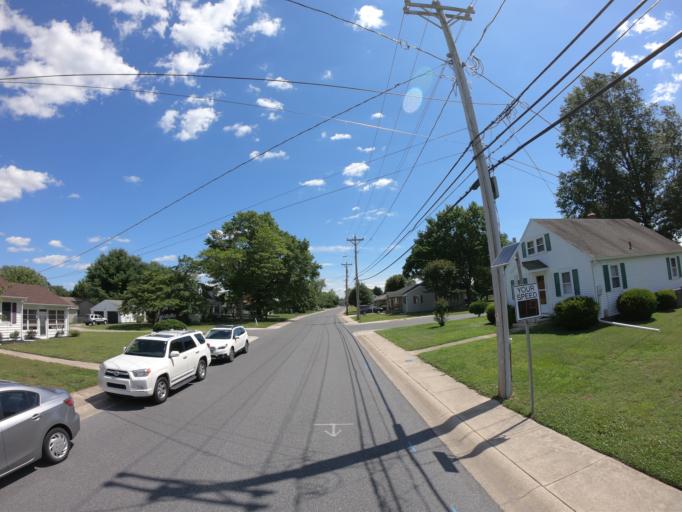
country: US
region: Delaware
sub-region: Sussex County
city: Milford
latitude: 38.9226
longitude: -75.4276
